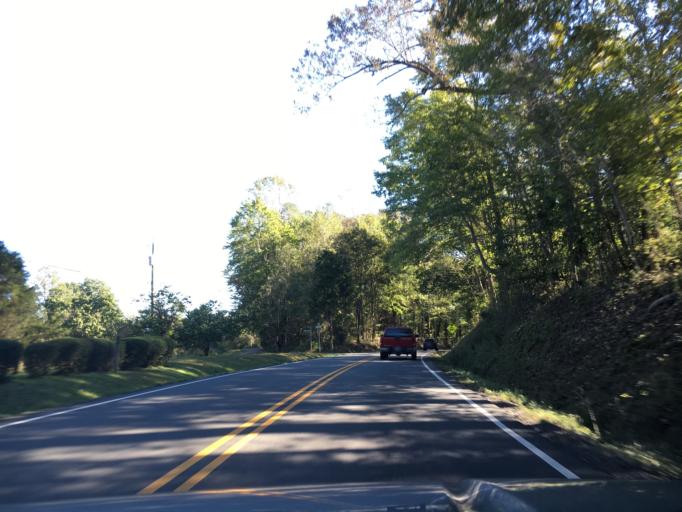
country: US
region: Virginia
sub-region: Goochland County
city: Goochland
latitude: 37.7001
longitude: -77.8382
